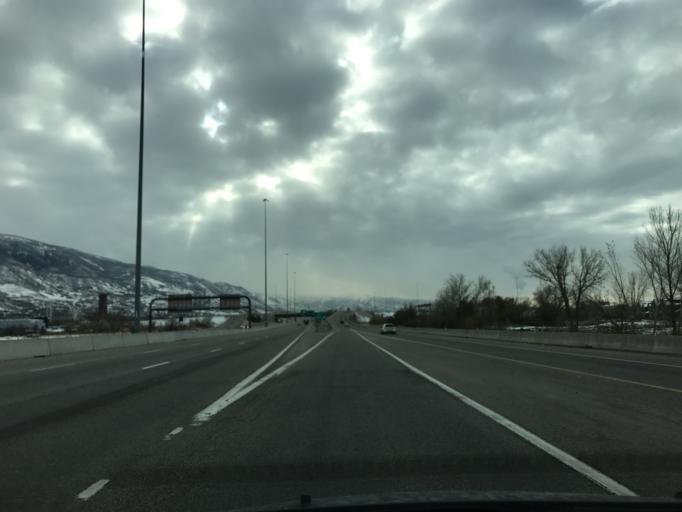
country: US
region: Utah
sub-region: Davis County
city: Farmington
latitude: 40.9963
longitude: -111.9057
